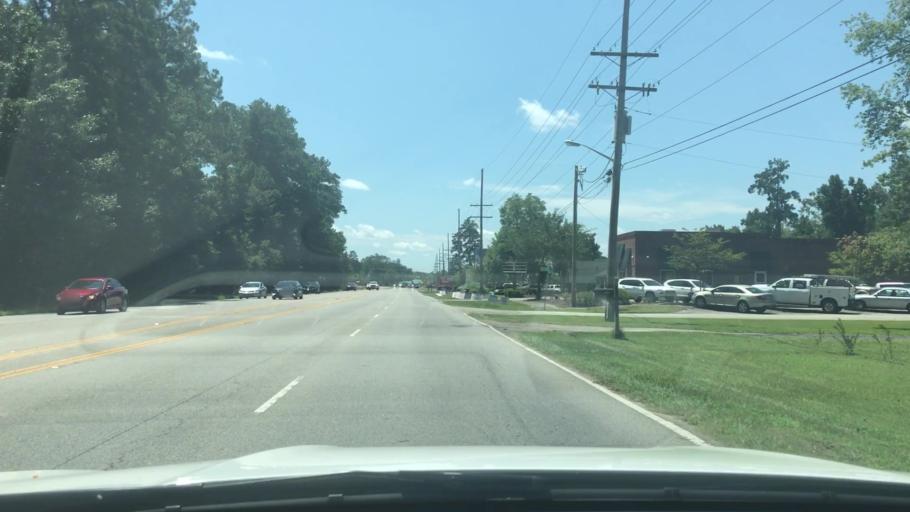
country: US
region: South Carolina
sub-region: Horry County
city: Conway
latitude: 33.8711
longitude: -79.0519
